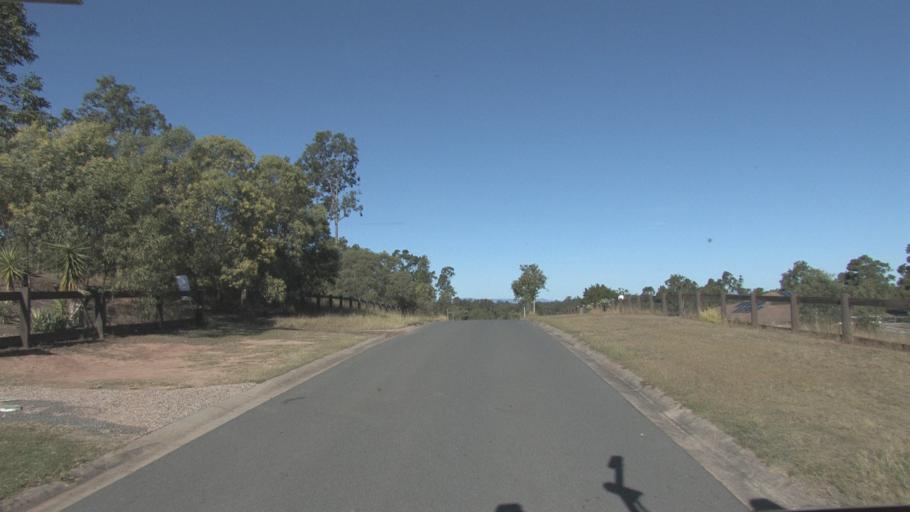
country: AU
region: Queensland
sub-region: Ipswich
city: Springfield Lakes
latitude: -27.7209
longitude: 152.9223
